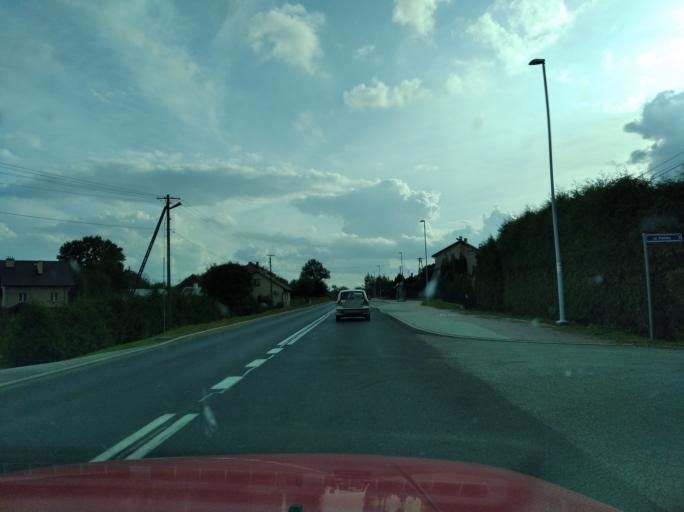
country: PL
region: Subcarpathian Voivodeship
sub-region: Powiat jaroslawski
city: Pawlosiow
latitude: 49.9941
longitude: 22.6654
